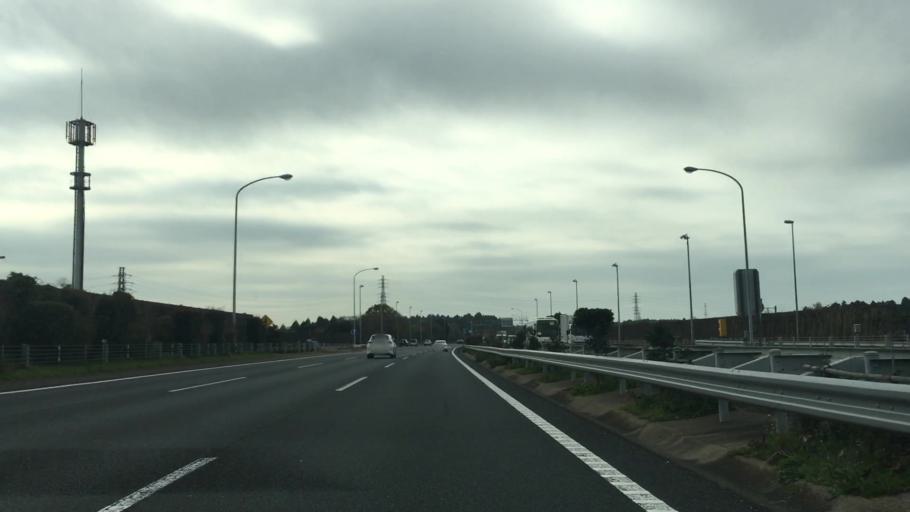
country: JP
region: Chiba
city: Narita
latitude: 35.7433
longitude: 140.3108
